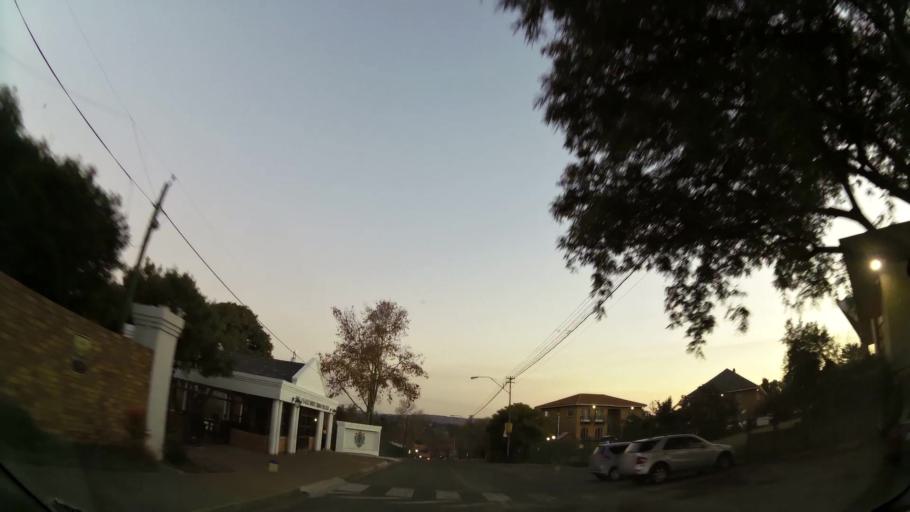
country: ZA
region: Gauteng
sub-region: City of Johannesburg Metropolitan Municipality
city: Johannesburg
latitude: -26.1421
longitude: 28.0029
